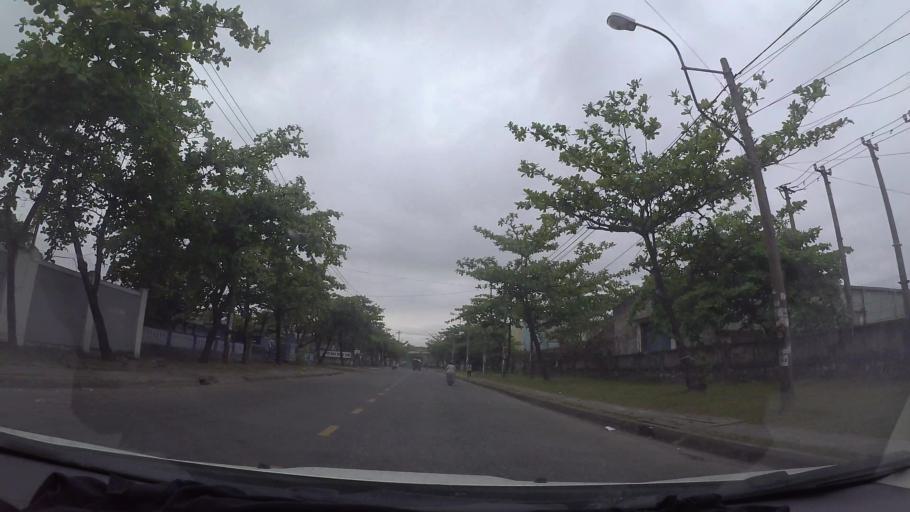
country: VN
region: Da Nang
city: Lien Chieu
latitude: 16.0827
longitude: 108.1405
